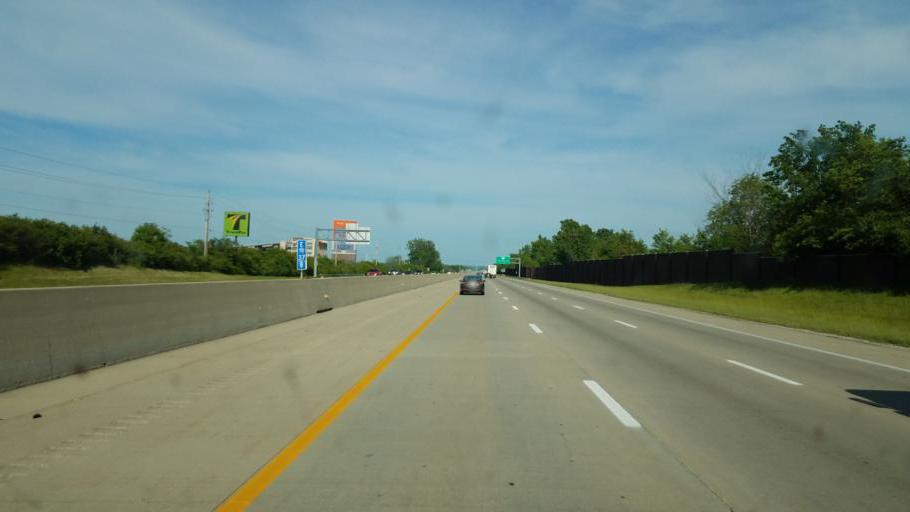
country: US
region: Ohio
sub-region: Montgomery County
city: Huber Heights
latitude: 39.8686
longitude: -84.1162
